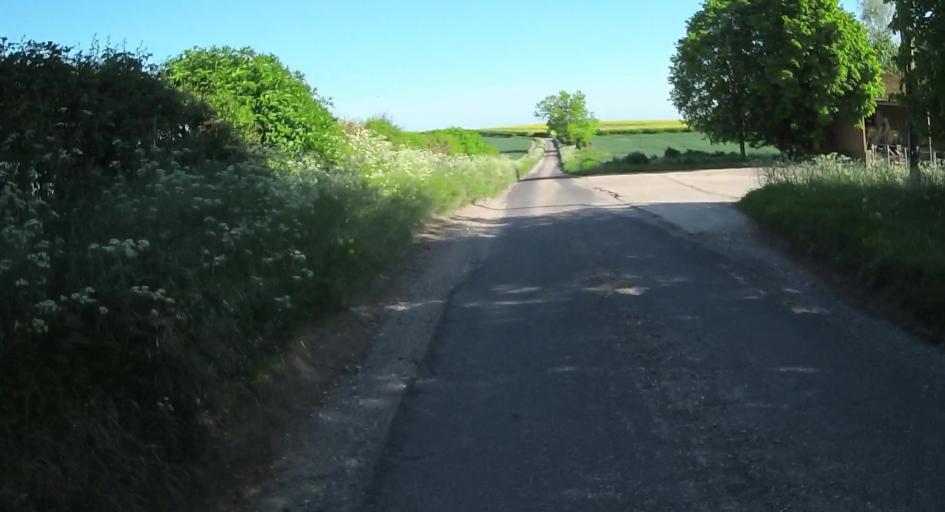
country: GB
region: England
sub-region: Hampshire
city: Overton
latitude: 51.1702
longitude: -1.1950
